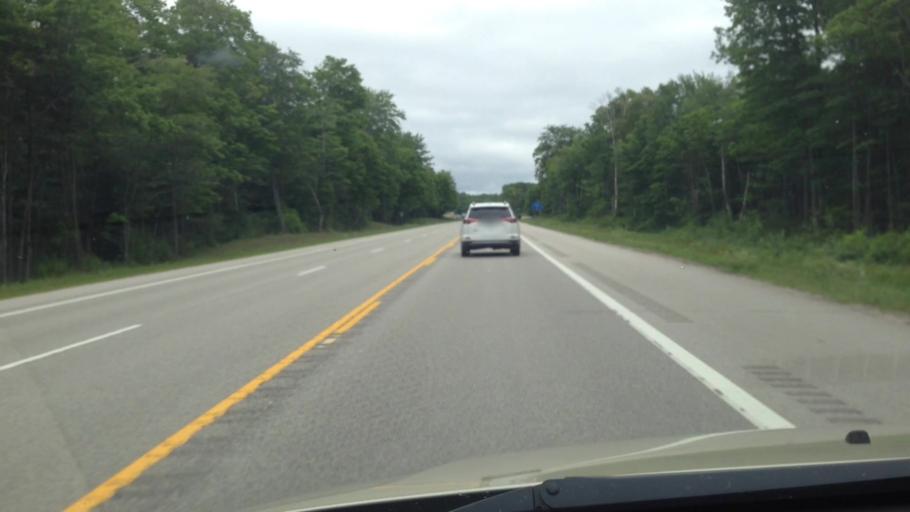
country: US
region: Michigan
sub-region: Luce County
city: Newberry
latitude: 46.0653
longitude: -85.1847
